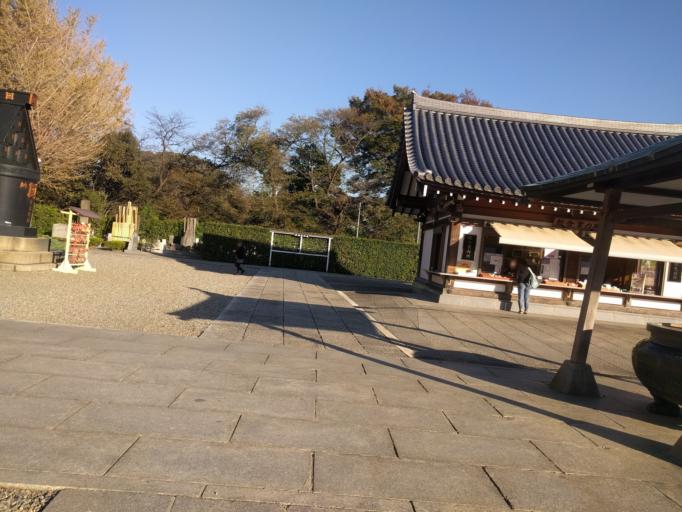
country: JP
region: Kanagawa
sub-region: Kawasaki-shi
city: Kawasaki
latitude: 35.5787
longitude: 139.7051
